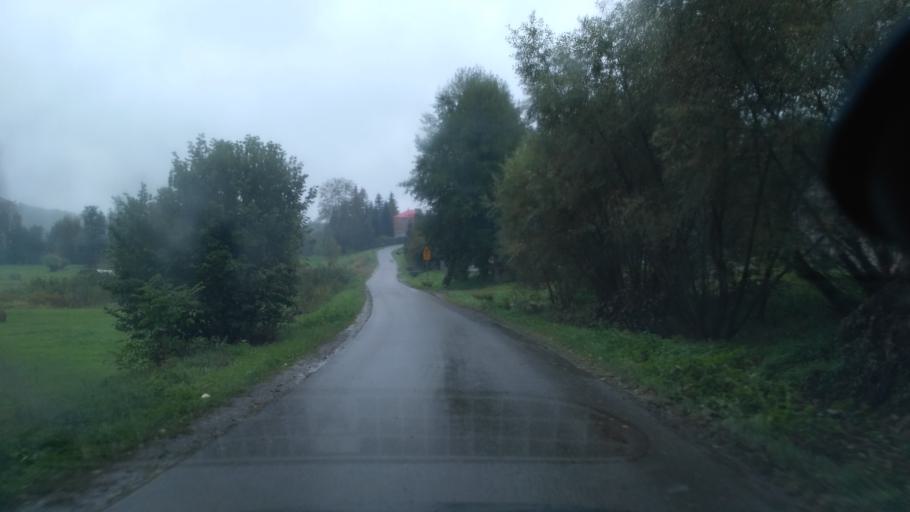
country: PL
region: Subcarpathian Voivodeship
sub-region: Powiat ropczycko-sedziszowski
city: Niedzwiada
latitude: 50.0202
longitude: 21.5416
